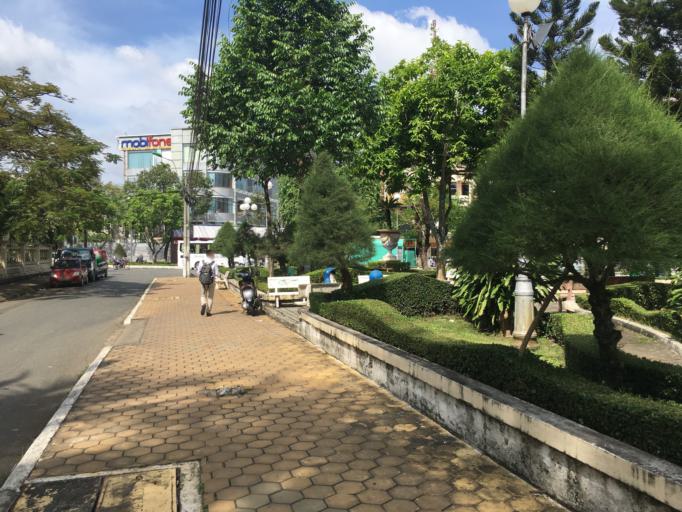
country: VN
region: Can Tho
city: Can Tho
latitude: 10.0353
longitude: 105.7871
